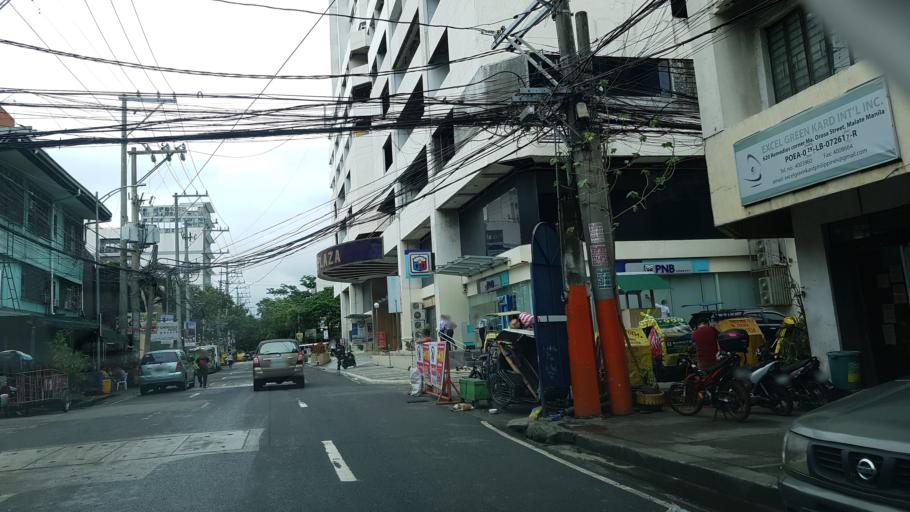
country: PH
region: Metro Manila
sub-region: City of Manila
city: Port Area
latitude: 14.5708
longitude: 120.9874
